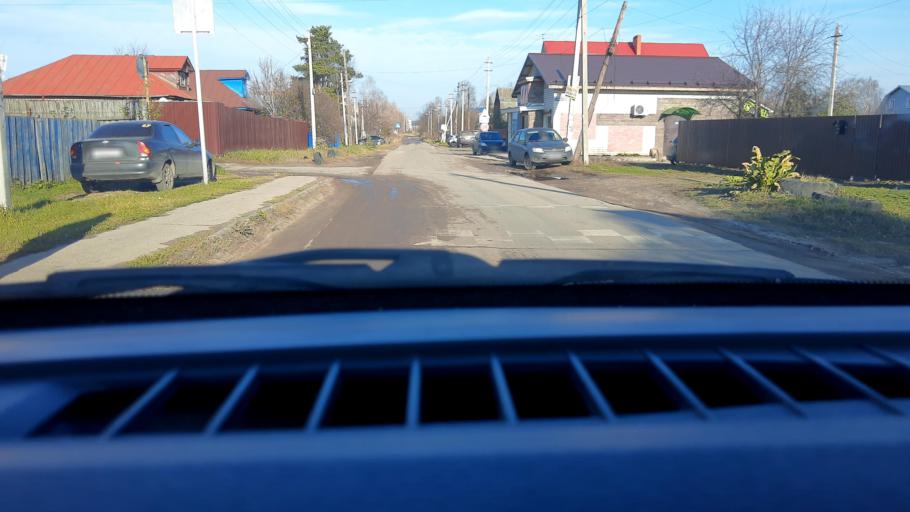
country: RU
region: Nizjnij Novgorod
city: Neklyudovo
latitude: 56.4131
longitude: 43.9796
